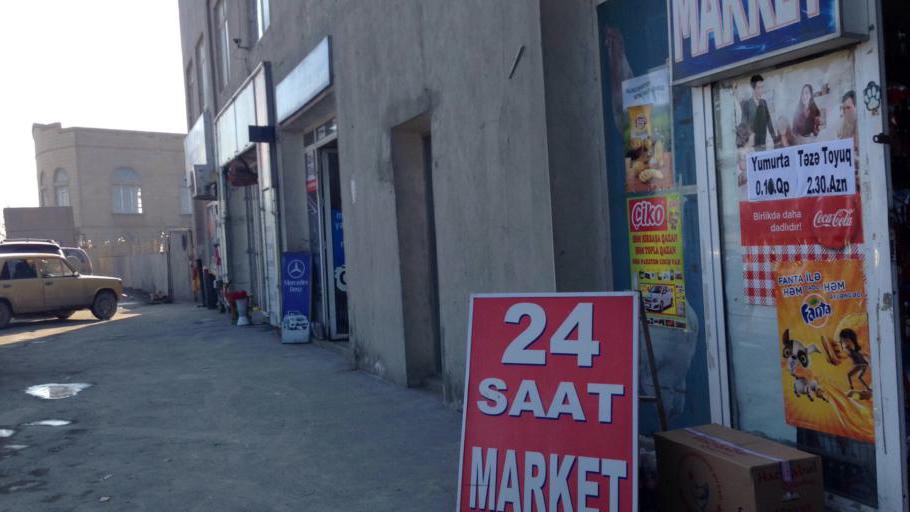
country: AZ
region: Baki
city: Sabuncu
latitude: 40.4449
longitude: 49.9338
